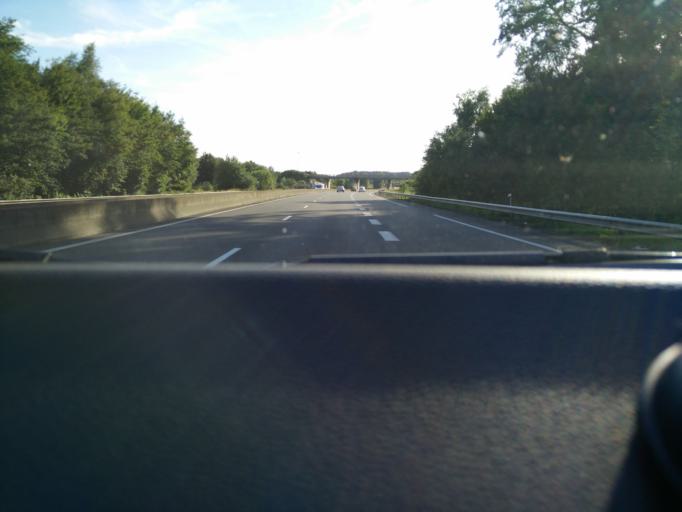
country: FR
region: Nord-Pas-de-Calais
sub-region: Departement du Nord
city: Montigny-en-Ostrevent
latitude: 50.3805
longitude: 3.1839
